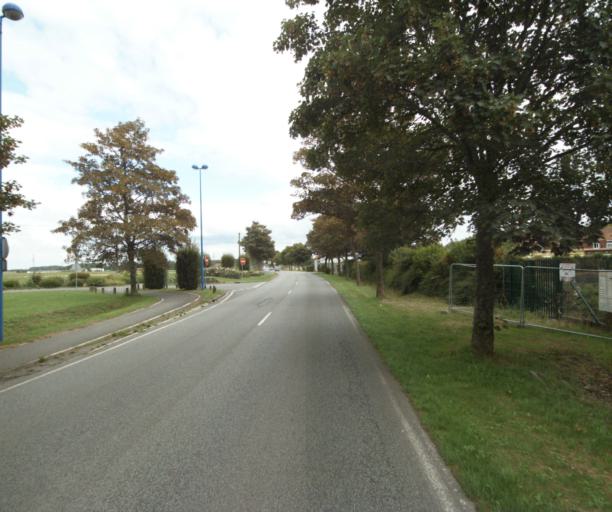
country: FR
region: Nord-Pas-de-Calais
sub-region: Departement du Nord
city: Villeneuve-d'Ascq
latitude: 50.6087
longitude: 3.1729
